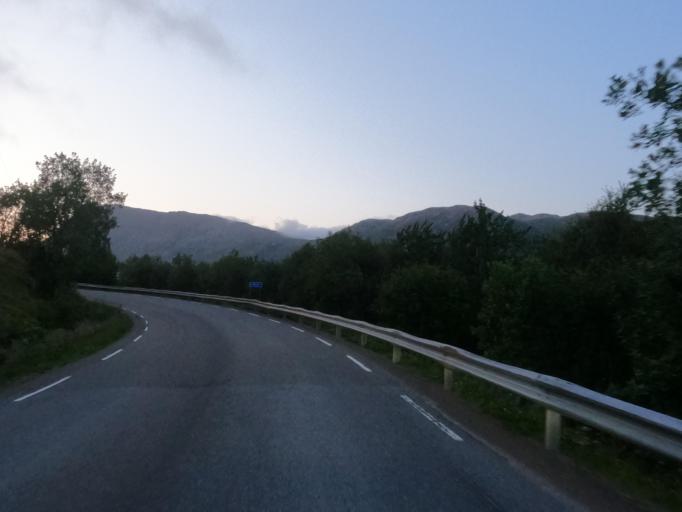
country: NO
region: Nordland
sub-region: Lodingen
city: Lodingen
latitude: 68.5652
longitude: 15.8011
